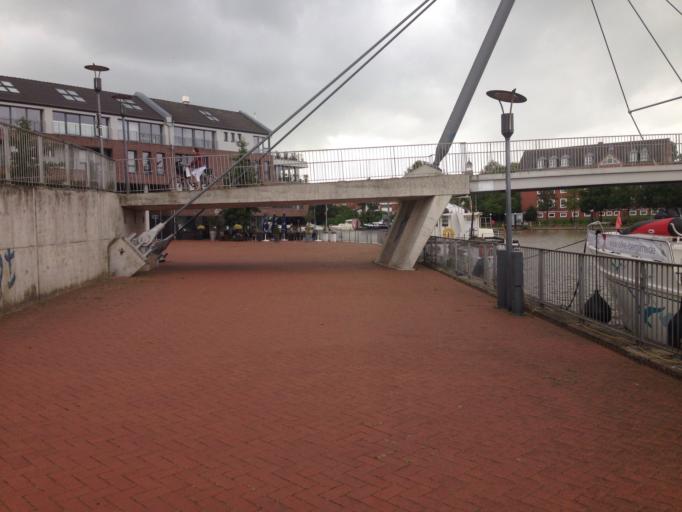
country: DE
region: Lower Saxony
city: Leer
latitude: 53.2284
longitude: 7.4570
